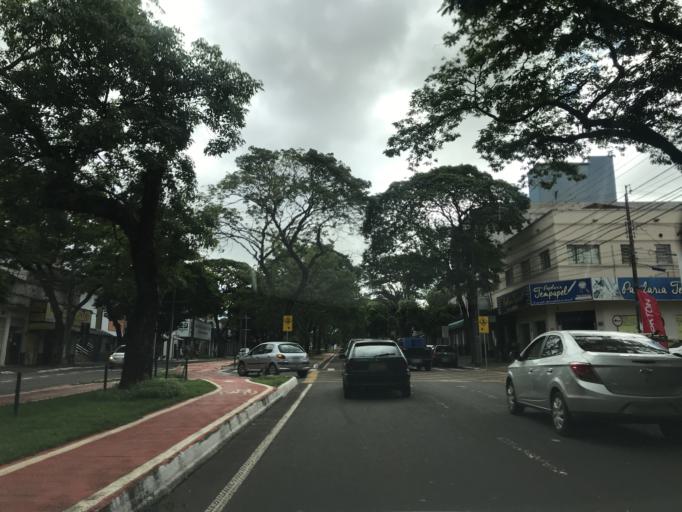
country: BR
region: Parana
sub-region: Maringa
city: Maringa
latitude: -23.4219
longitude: -51.9511
